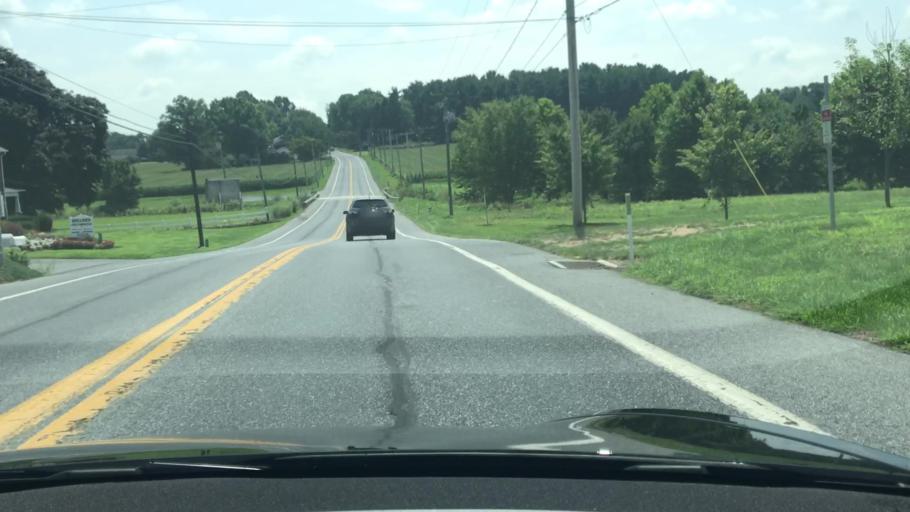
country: US
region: Pennsylvania
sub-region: Lancaster County
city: Landisville
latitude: 40.0847
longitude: -76.4090
